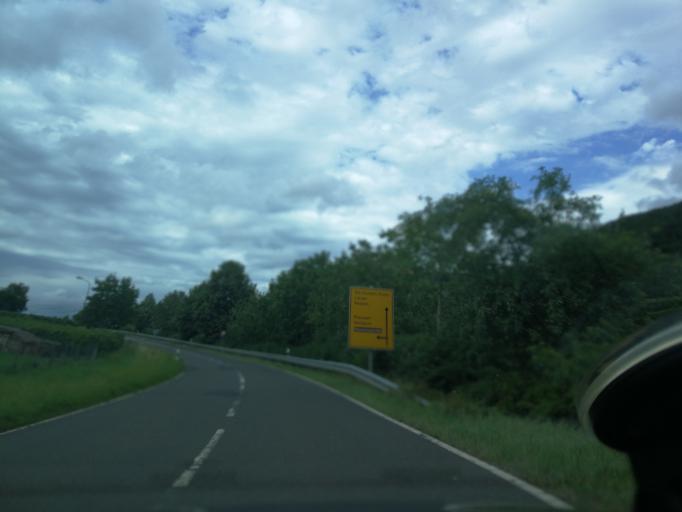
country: DE
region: Rheinland-Pfalz
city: Minheim
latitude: 49.8644
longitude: 6.9407
